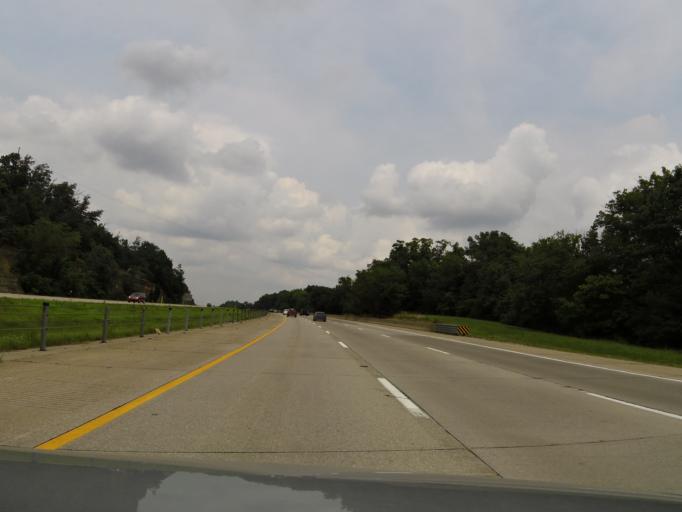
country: US
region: Kentucky
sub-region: Bullitt County
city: Shepherdsville
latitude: 38.0113
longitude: -85.6973
